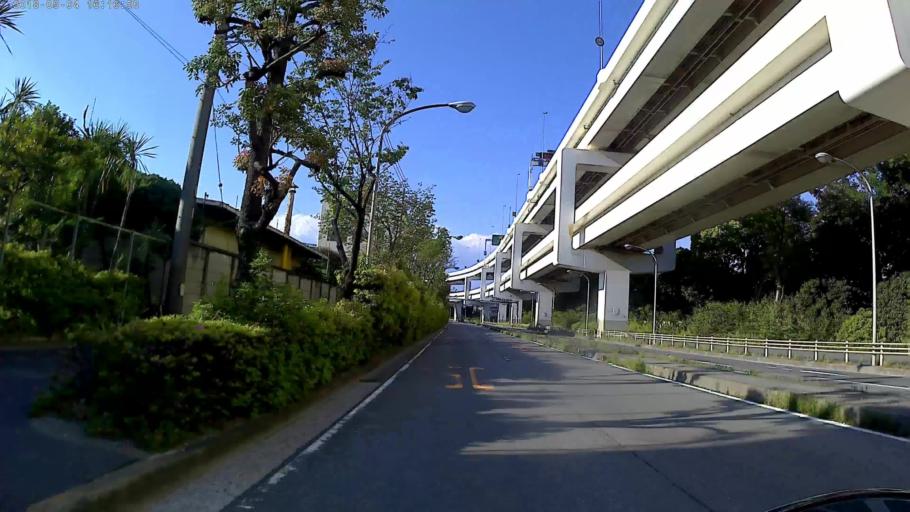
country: JP
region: Kanagawa
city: Yokohama
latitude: 35.4816
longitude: 139.6752
